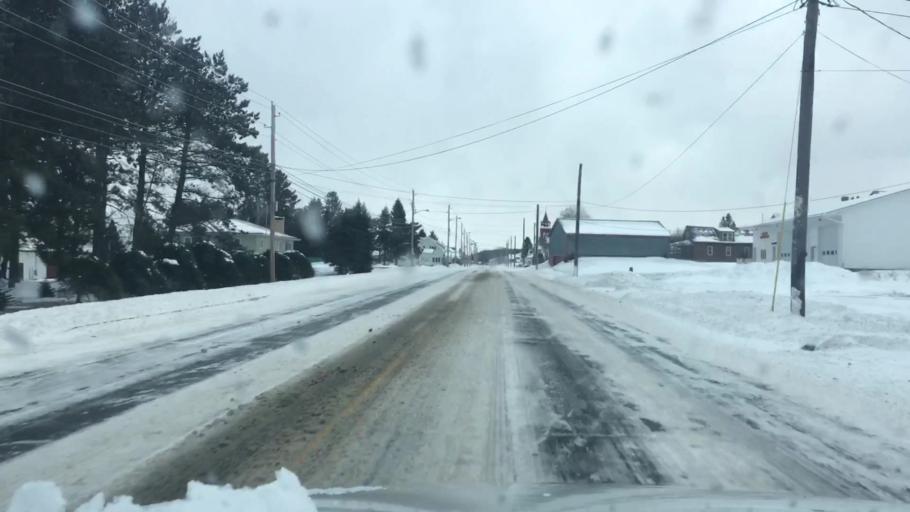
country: US
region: Maine
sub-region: Aroostook County
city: Madawaska
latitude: 47.3112
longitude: -68.1587
